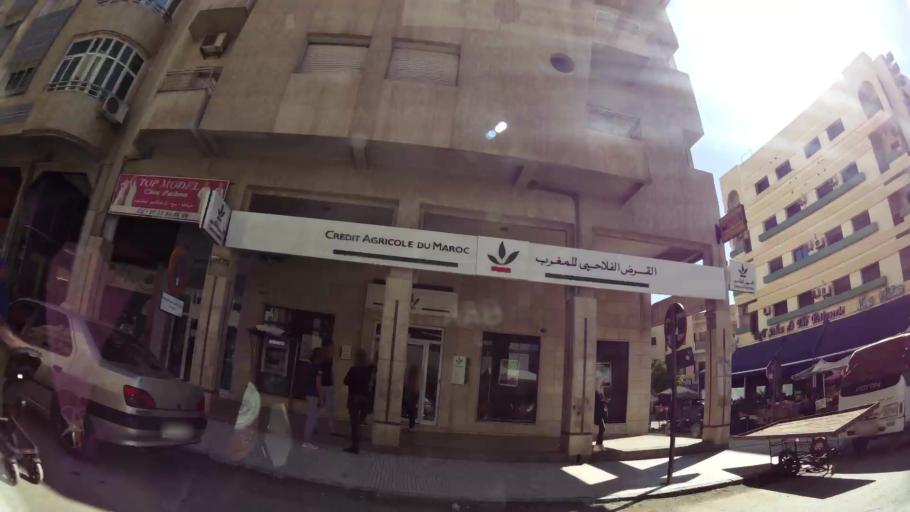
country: MA
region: Fes-Boulemane
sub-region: Fes
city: Fes
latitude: 34.0166
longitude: -4.9779
